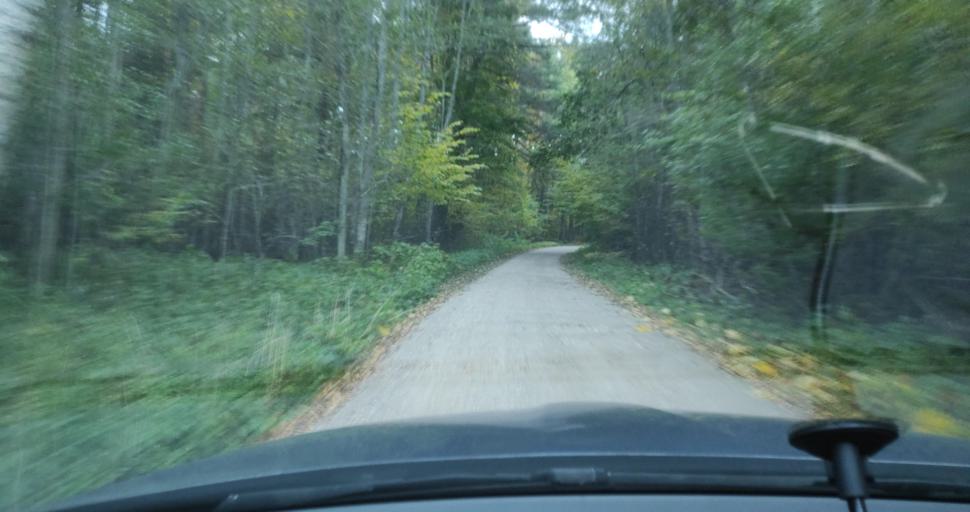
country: LV
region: Kandava
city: Kandava
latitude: 57.0214
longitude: 22.7591
